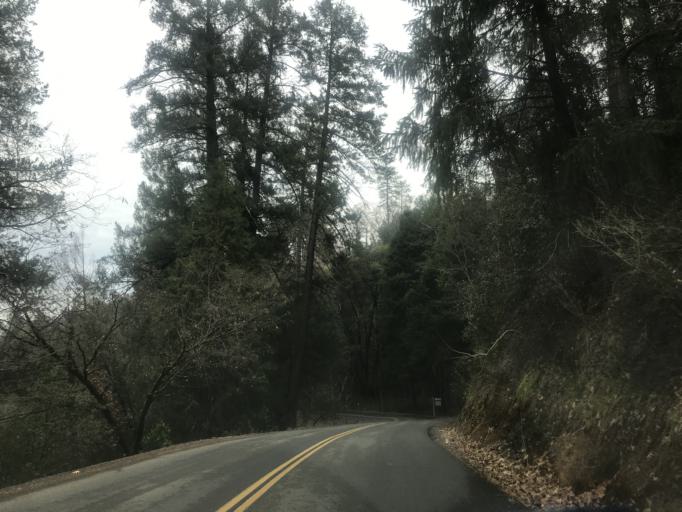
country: US
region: California
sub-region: El Dorado County
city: Placerville
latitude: 38.7287
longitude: -120.8166
